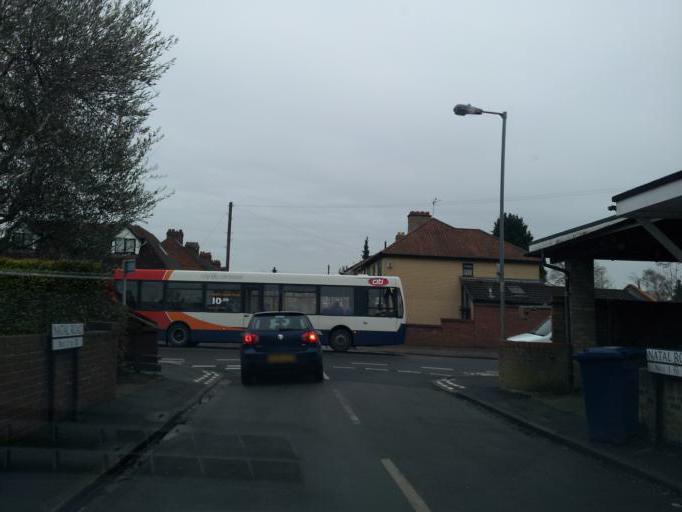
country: GB
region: England
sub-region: Cambridgeshire
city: Cambridge
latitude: 52.1953
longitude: 0.1555
